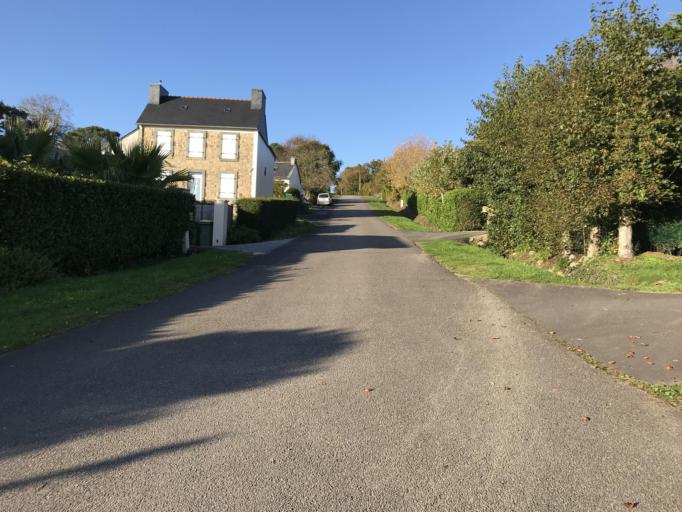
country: FR
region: Brittany
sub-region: Departement du Finistere
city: Hopital-Camfrout
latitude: 48.2985
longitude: -4.2238
